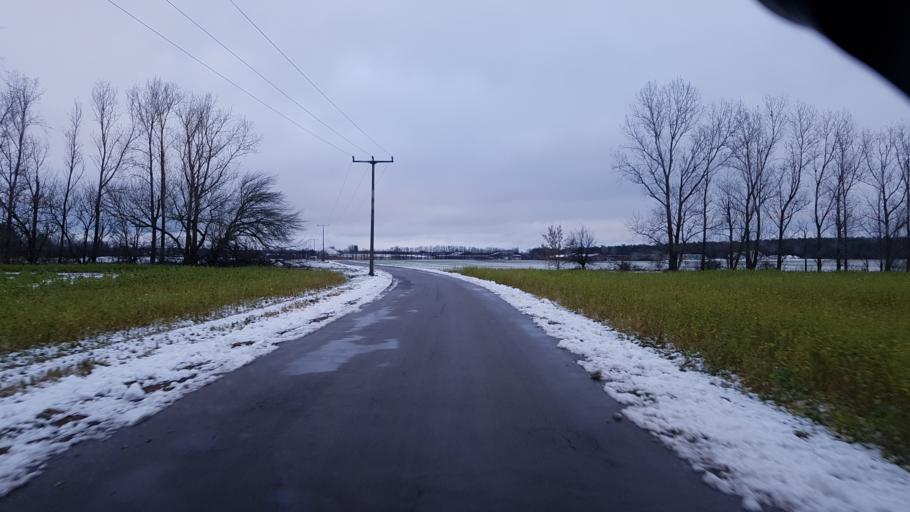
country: DE
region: Brandenburg
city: Luckau
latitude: 51.8094
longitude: 13.6880
